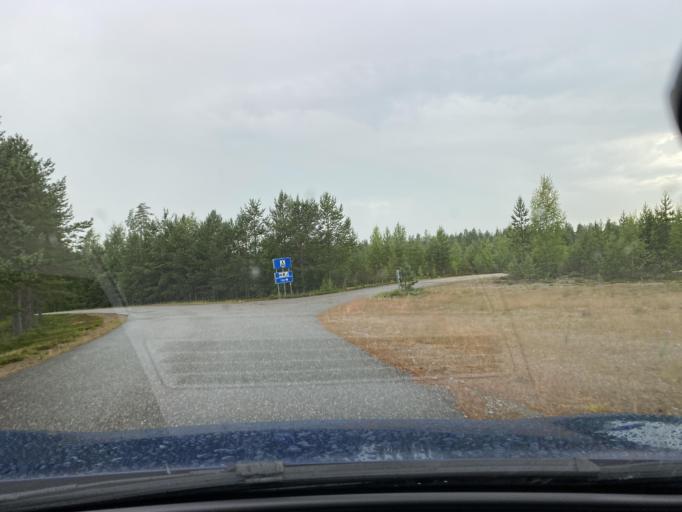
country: FI
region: Central Ostrobothnia
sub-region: Kaustinen
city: Halsua
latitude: 63.4201
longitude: 23.9766
